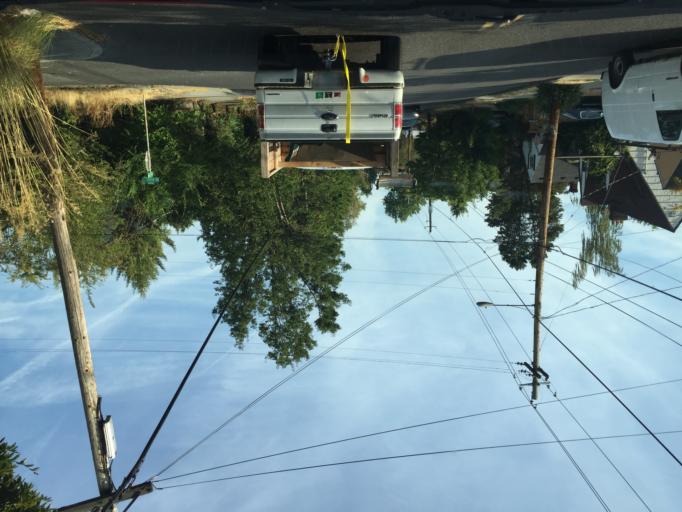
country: US
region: Oregon
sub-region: Multnomah County
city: Portland
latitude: 45.5445
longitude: -122.6307
